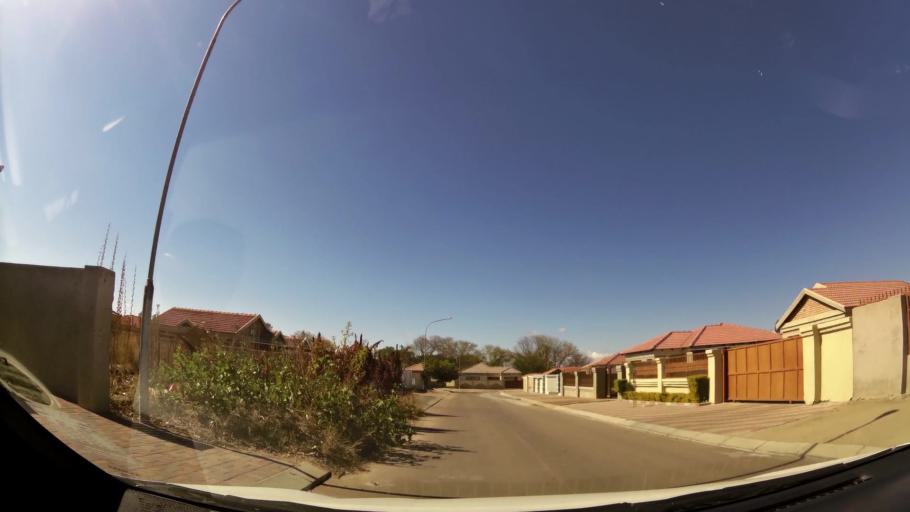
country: ZA
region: Limpopo
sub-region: Capricorn District Municipality
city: Polokwane
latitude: -23.8595
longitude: 29.4256
